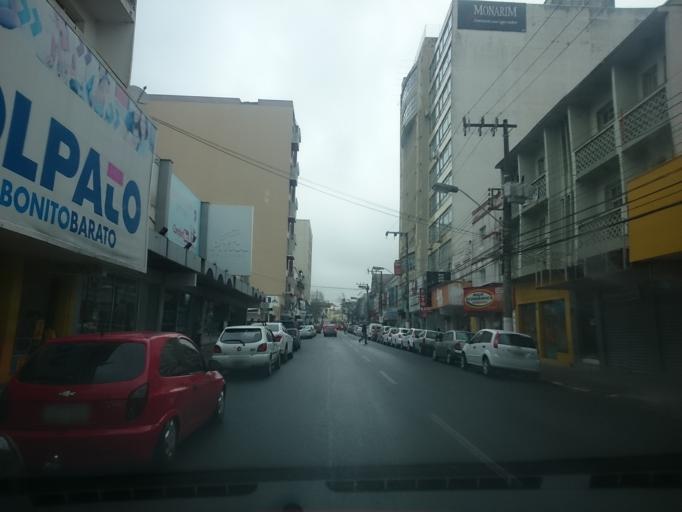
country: BR
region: Santa Catarina
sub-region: Lages
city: Lages
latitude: -27.8137
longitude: -50.3259
